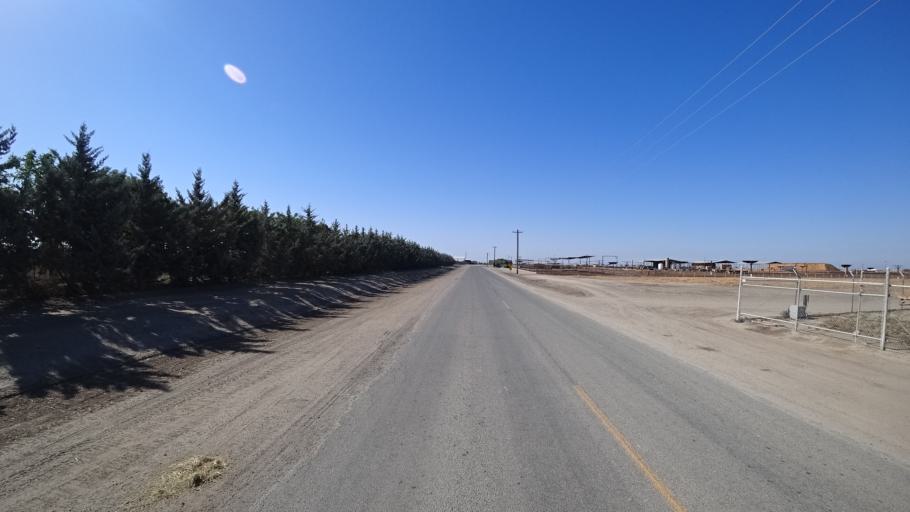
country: US
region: California
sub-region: Kings County
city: Corcoran
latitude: 36.1843
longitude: -119.5644
